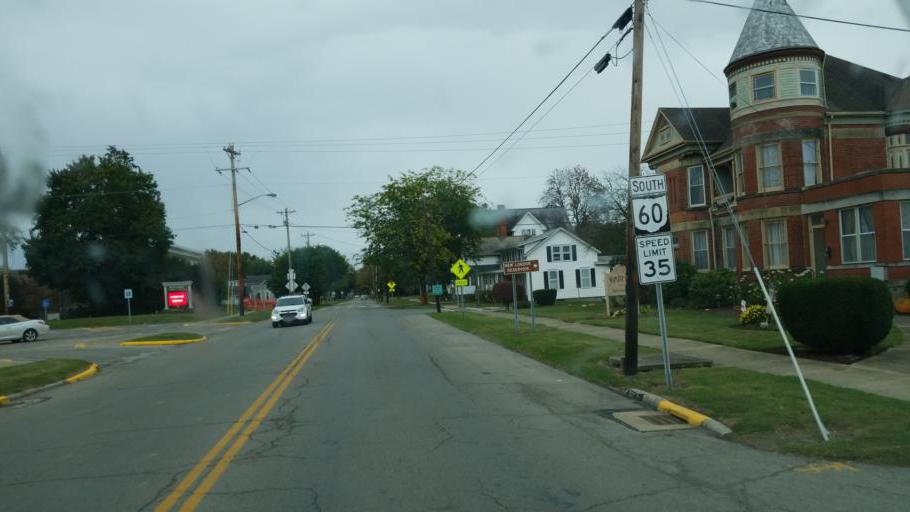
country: US
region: Ohio
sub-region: Huron County
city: New London
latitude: 41.0845
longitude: -82.3990
